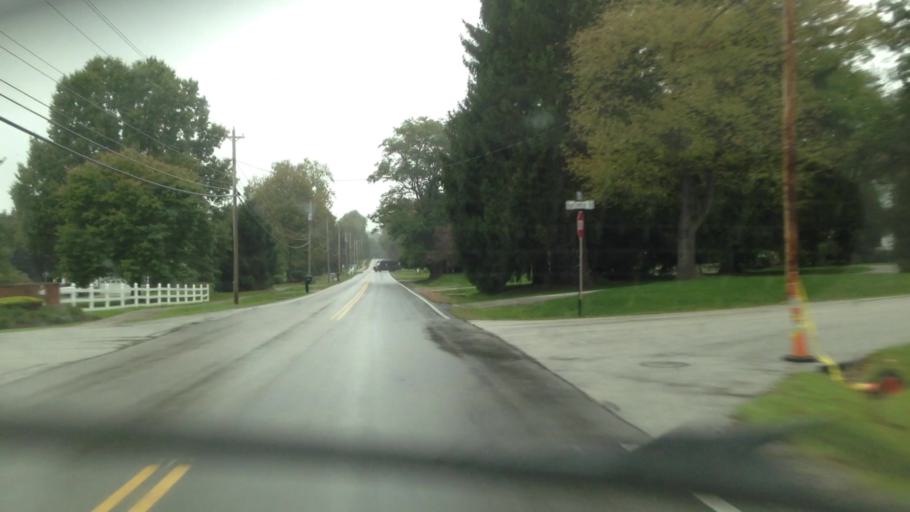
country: US
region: Ohio
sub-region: Summit County
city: Hudson
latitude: 41.2617
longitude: -81.4033
